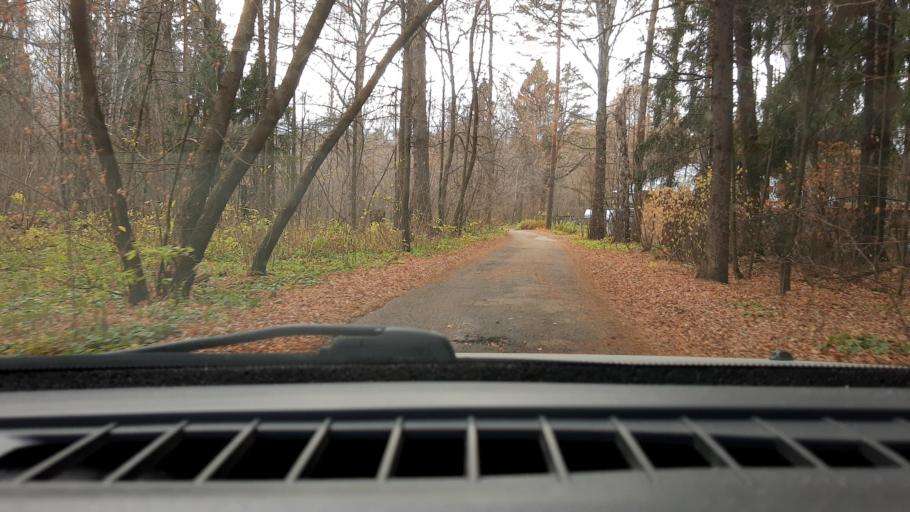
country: RU
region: Nizjnij Novgorod
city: Kstovo
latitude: 56.1698
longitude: 44.1316
